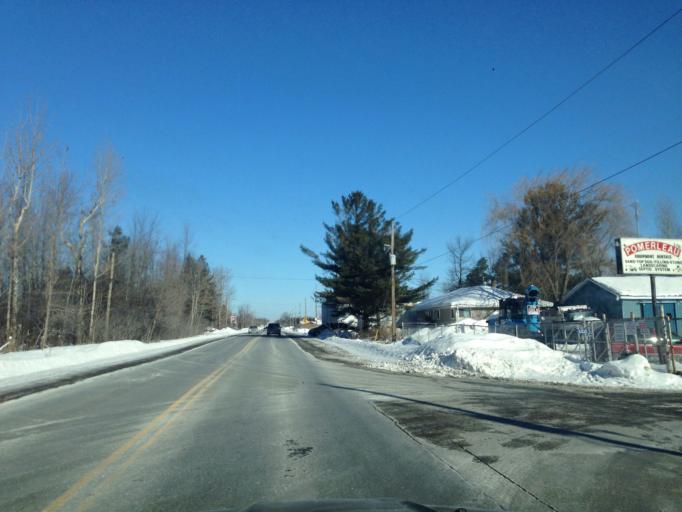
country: CA
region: Ontario
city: Clarence-Rockland
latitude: 45.3415
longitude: -75.4414
